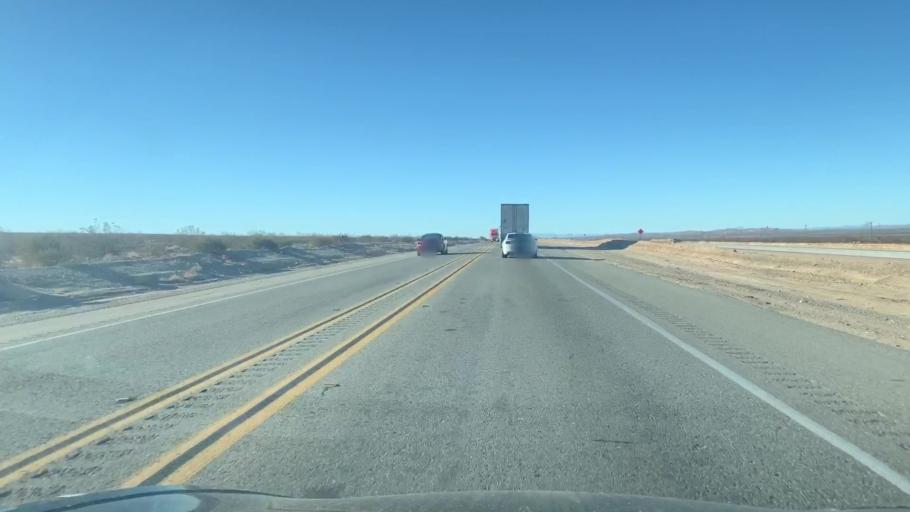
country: US
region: California
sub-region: Kern County
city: Boron
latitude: 34.9785
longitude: -117.4748
